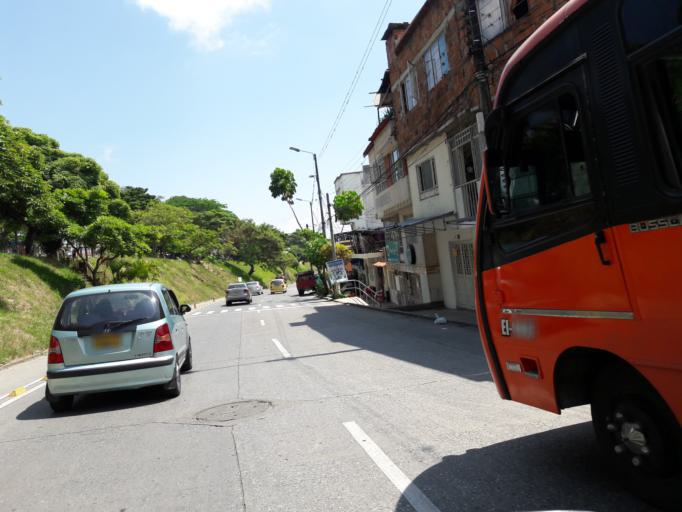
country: CO
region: Tolima
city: Ibague
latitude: 4.4364
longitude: -75.2220
